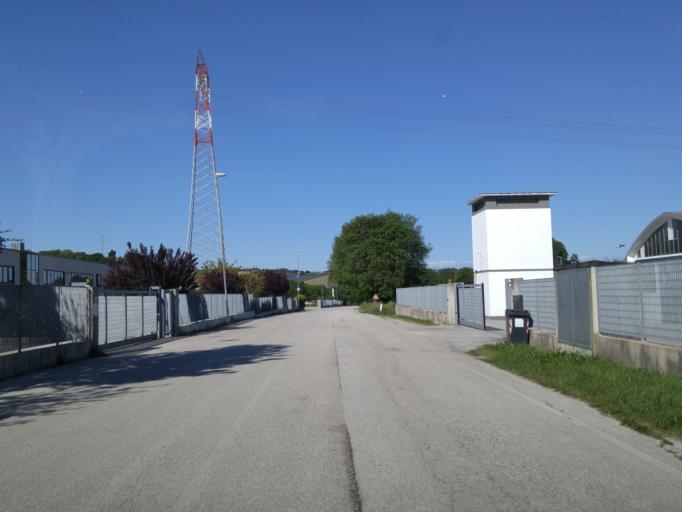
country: IT
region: The Marches
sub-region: Provincia di Pesaro e Urbino
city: Mombaroccio
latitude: 43.8311
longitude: 12.8626
